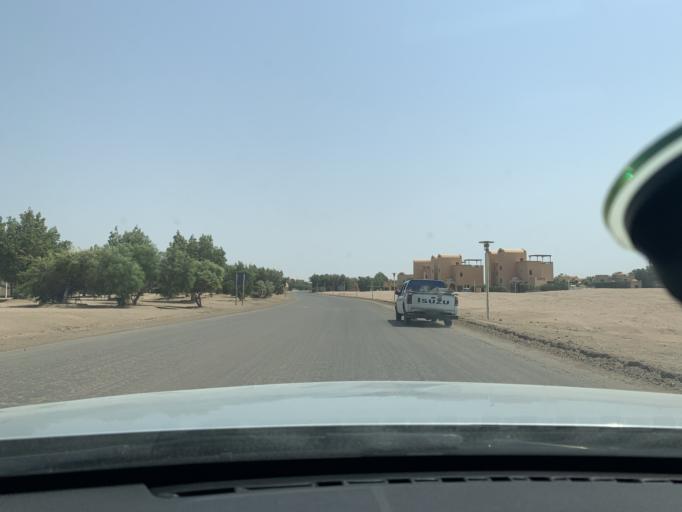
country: EG
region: Red Sea
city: El Gouna
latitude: 27.3893
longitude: 33.6692
